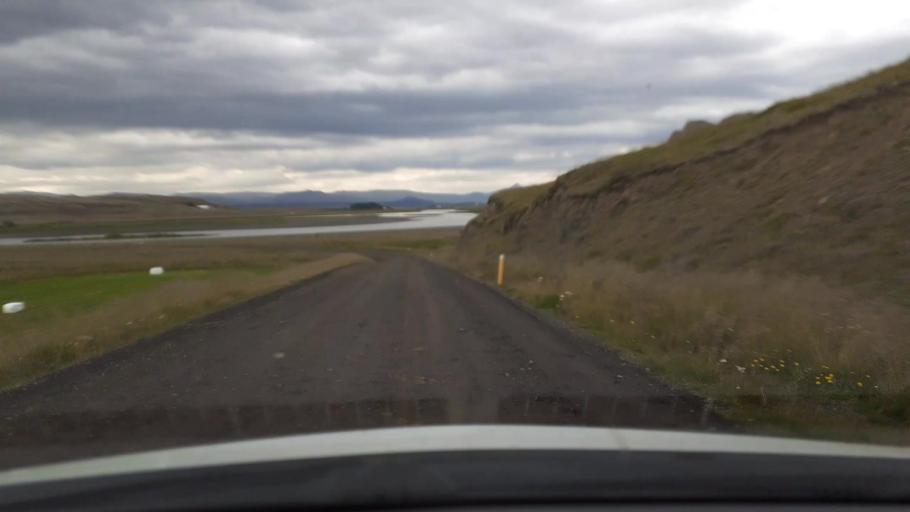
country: IS
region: West
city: Borgarnes
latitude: 64.6017
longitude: -21.6975
